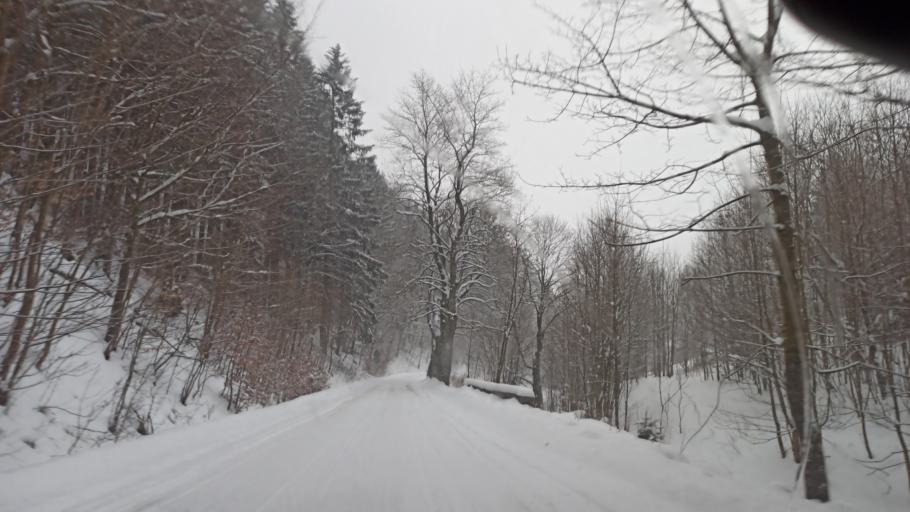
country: PL
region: Lower Silesian Voivodeship
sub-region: Powiat klodzki
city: Ludwikowice Klodzkie
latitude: 50.6602
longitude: 16.4785
